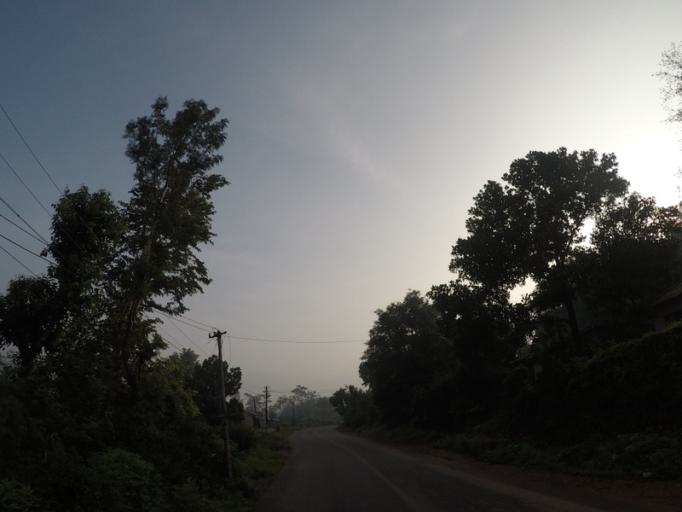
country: IN
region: Karnataka
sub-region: Chikmagalur
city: Chikmagalur
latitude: 13.3968
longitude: 75.7813
